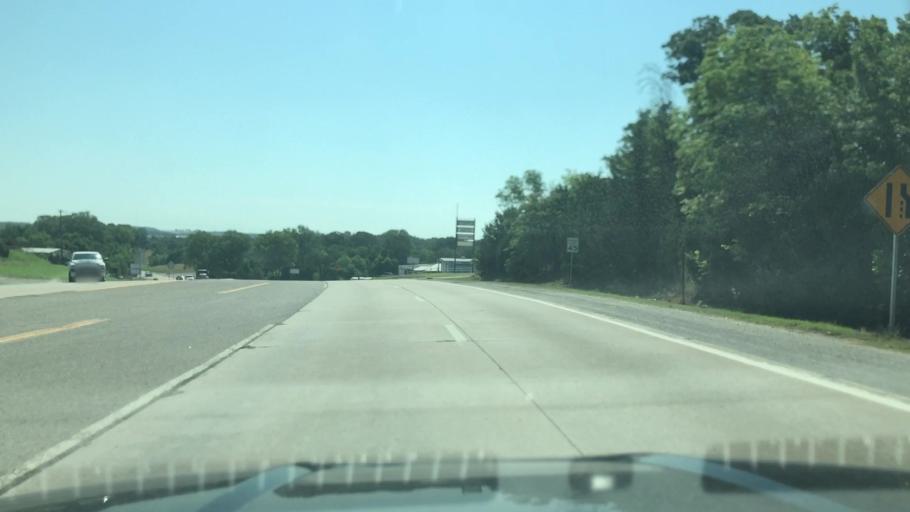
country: US
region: Oklahoma
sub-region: Creek County
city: Drumright
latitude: 35.9869
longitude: -96.5828
